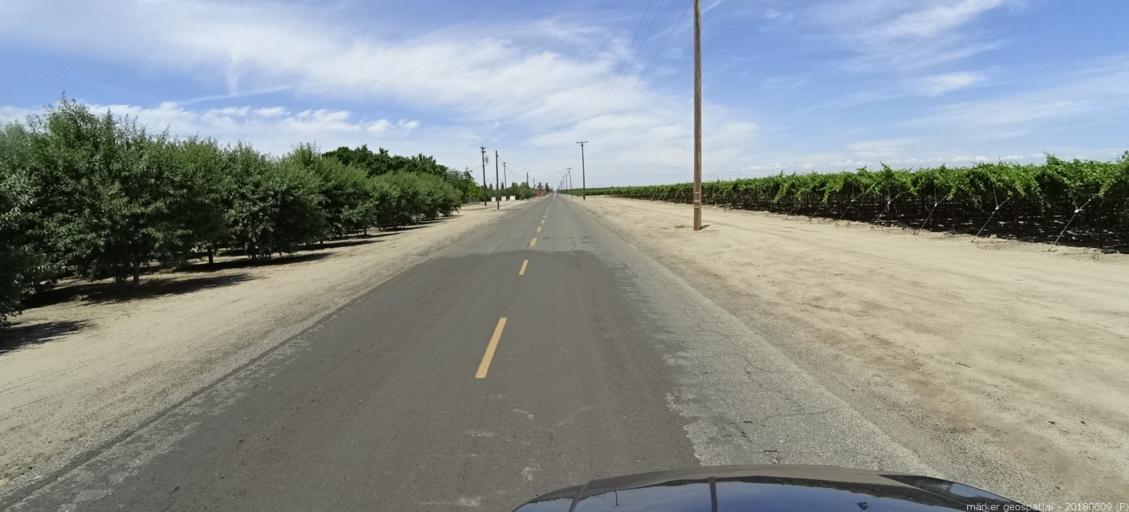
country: US
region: California
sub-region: Madera County
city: Parkwood
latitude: 36.8713
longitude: -120.0922
